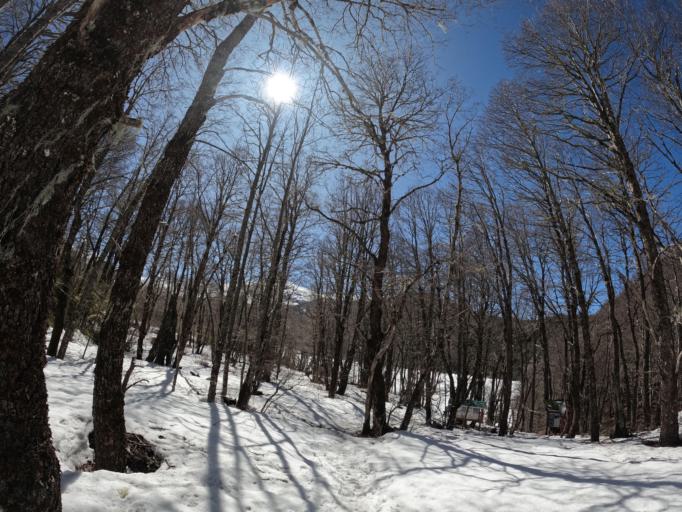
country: CL
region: Araucania
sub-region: Provincia de Cautin
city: Vilcun
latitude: -38.6494
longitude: -71.6184
